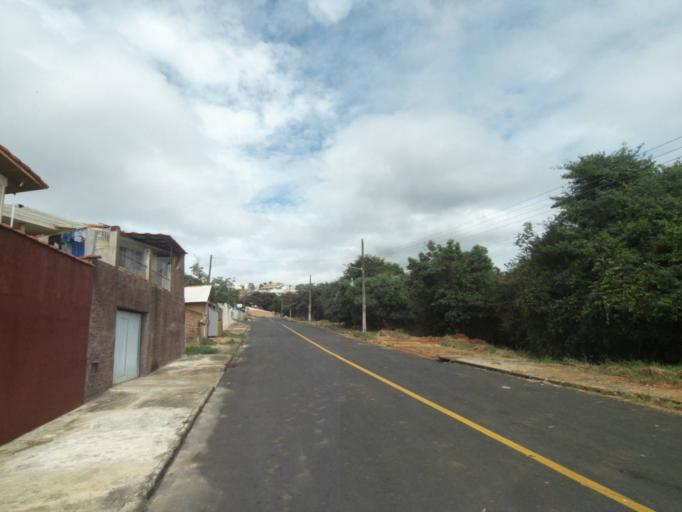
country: BR
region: Parana
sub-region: Telemaco Borba
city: Telemaco Borba
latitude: -24.3325
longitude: -50.6411
